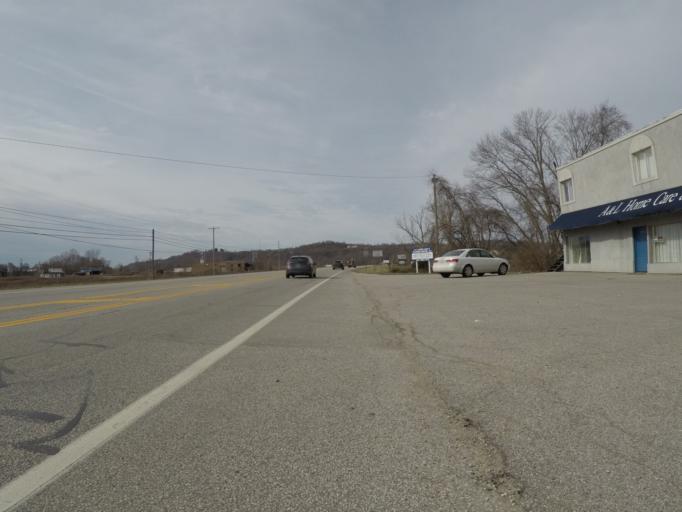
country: US
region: West Virginia
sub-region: Cabell County
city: Huntington
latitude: 38.4396
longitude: -82.3896
